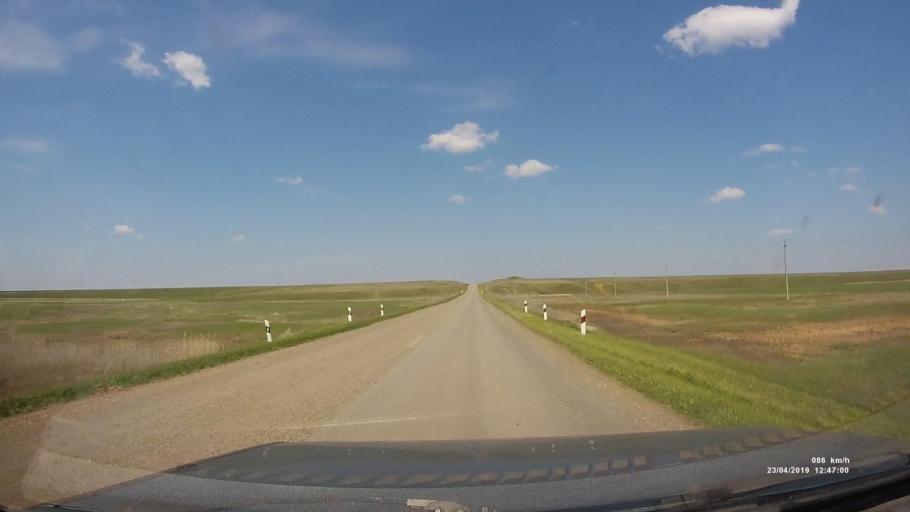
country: RU
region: Kalmykiya
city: Yashalta
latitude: 46.5065
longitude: 42.6385
